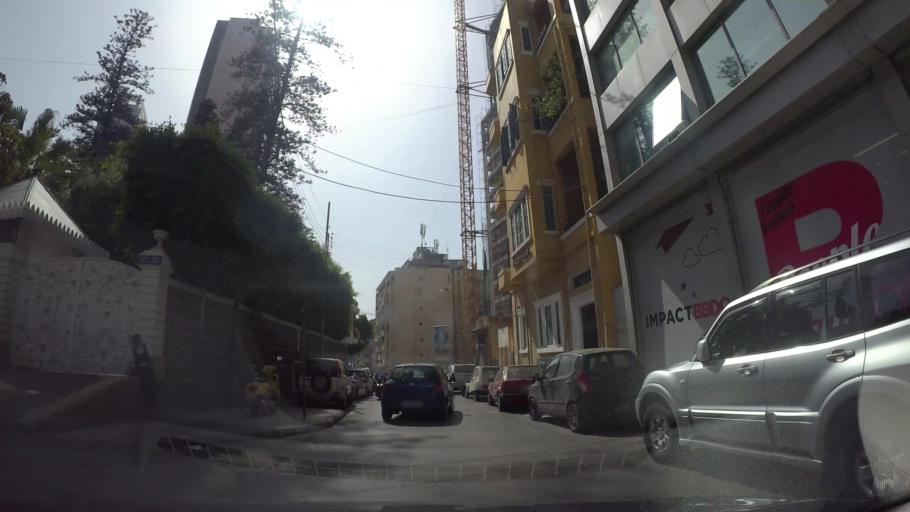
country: LB
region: Beyrouth
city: Ra's Bayrut
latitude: 33.8991
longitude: 35.4918
